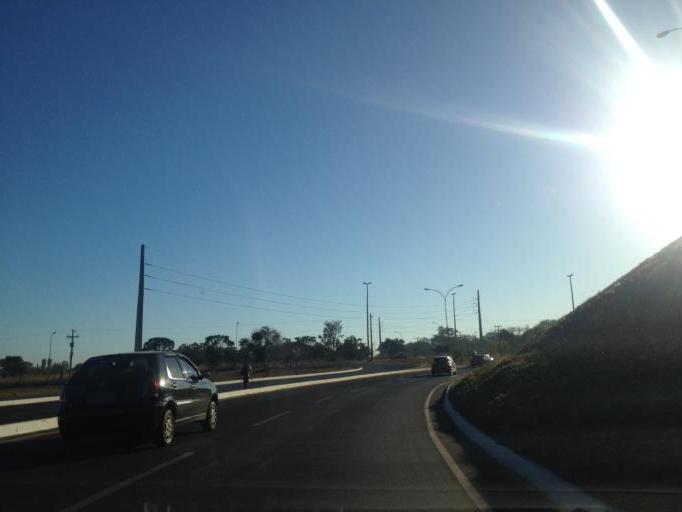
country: BR
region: Federal District
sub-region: Brasilia
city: Brasilia
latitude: -15.7748
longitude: -47.9392
